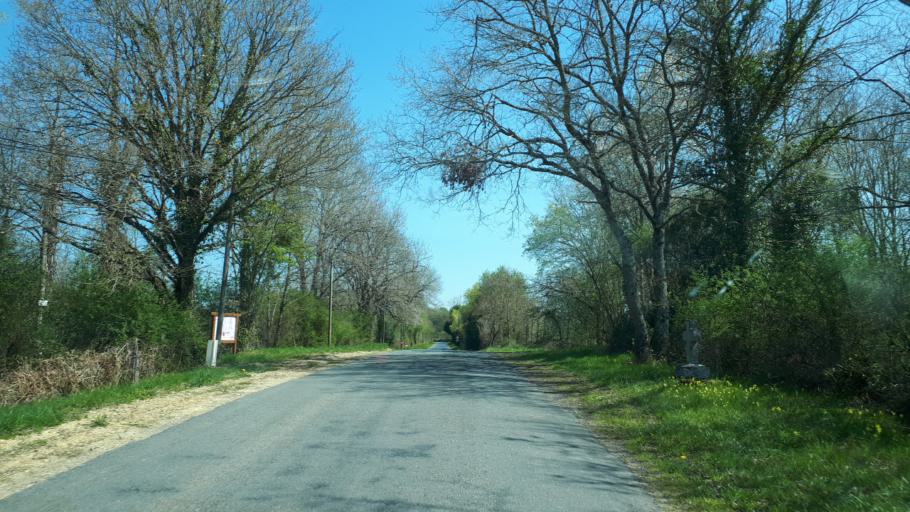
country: FR
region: Centre
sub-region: Departement du Cher
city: Henrichemont
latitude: 47.3047
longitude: 2.4968
